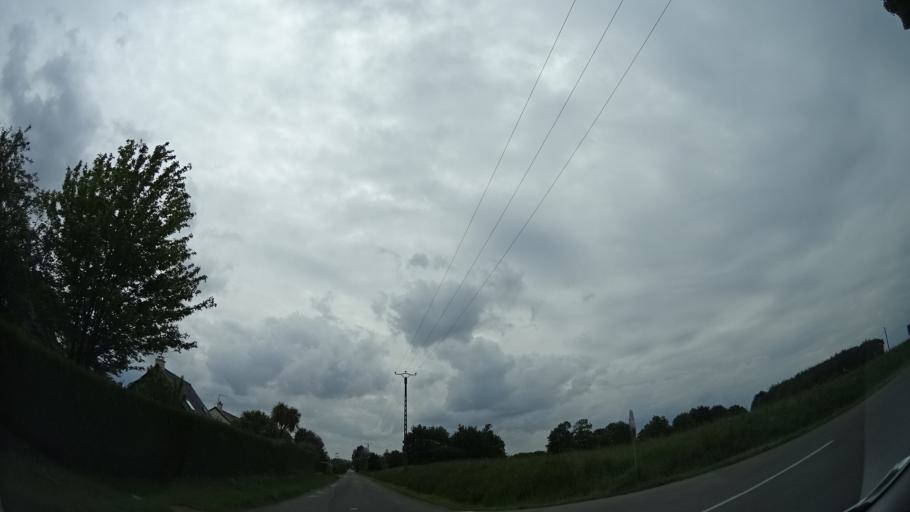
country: FR
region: Brittany
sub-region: Departement d'Ille-et-Vilaine
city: Tinteniac
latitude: 48.2753
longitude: -1.8520
